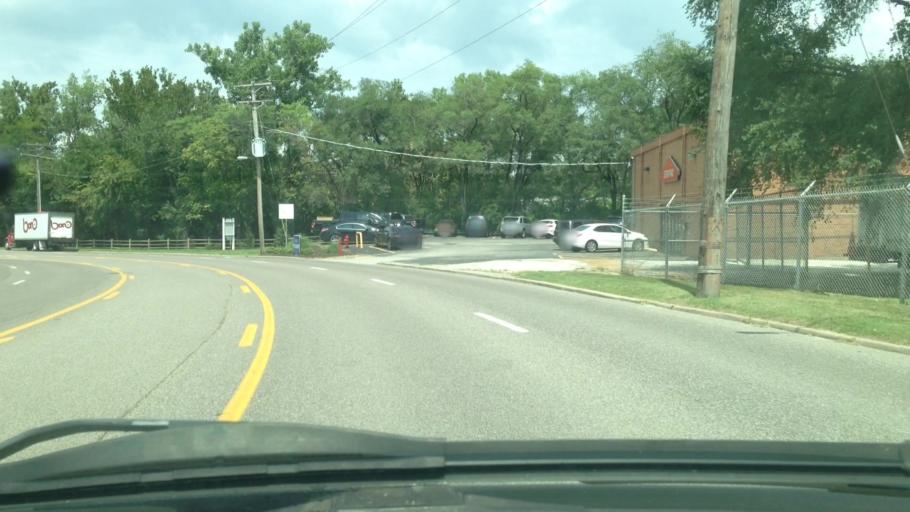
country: US
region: Missouri
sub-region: Saint Louis County
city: Maplewood
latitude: 38.5996
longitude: -90.3254
